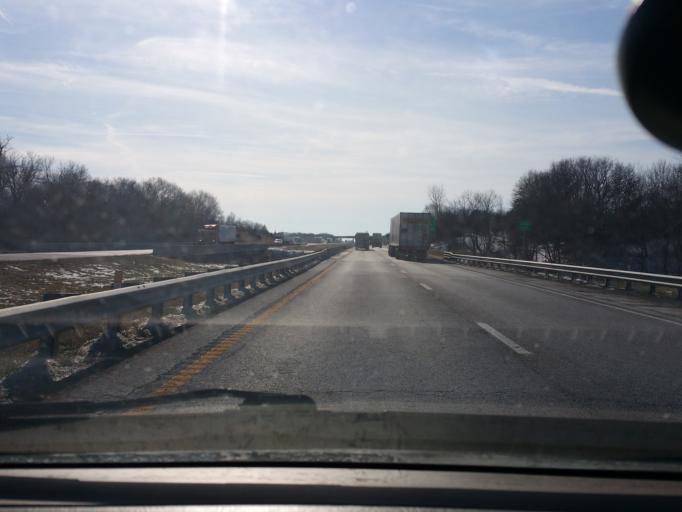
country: US
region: Missouri
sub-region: Clinton County
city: Cameron
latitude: 39.6746
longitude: -94.2340
